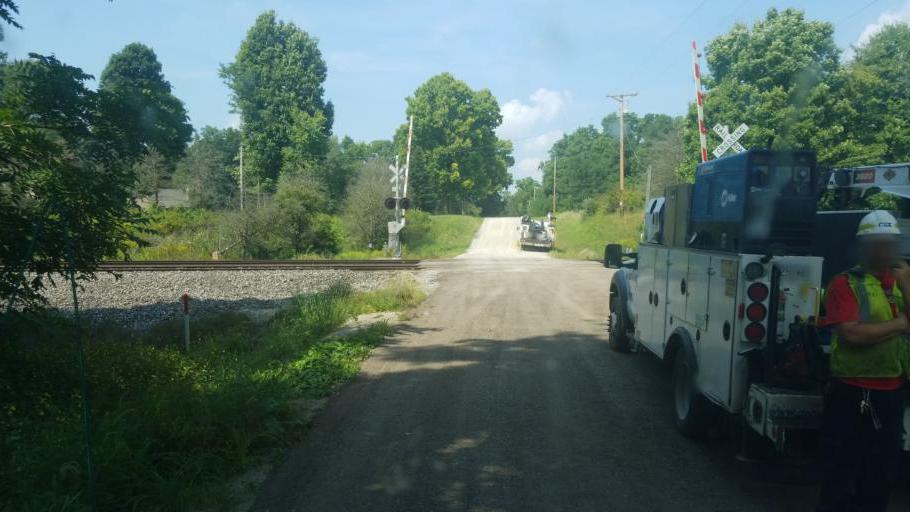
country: US
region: Ohio
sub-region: Huron County
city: New London
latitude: 41.0574
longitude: -82.4097
